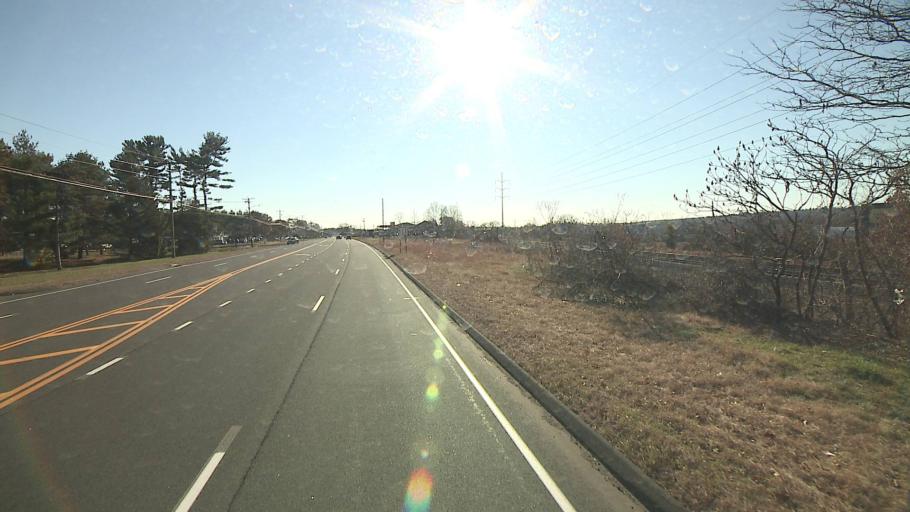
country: US
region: Connecticut
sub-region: New Haven County
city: Wallingford Center
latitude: 41.4240
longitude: -72.8392
